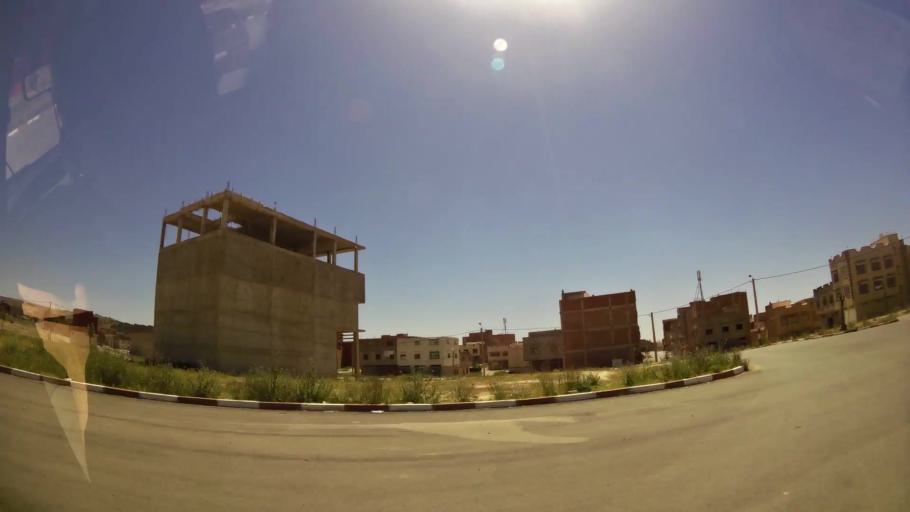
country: MA
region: Oriental
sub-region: Oujda-Angad
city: Oujda
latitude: 34.6580
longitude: -1.8725
